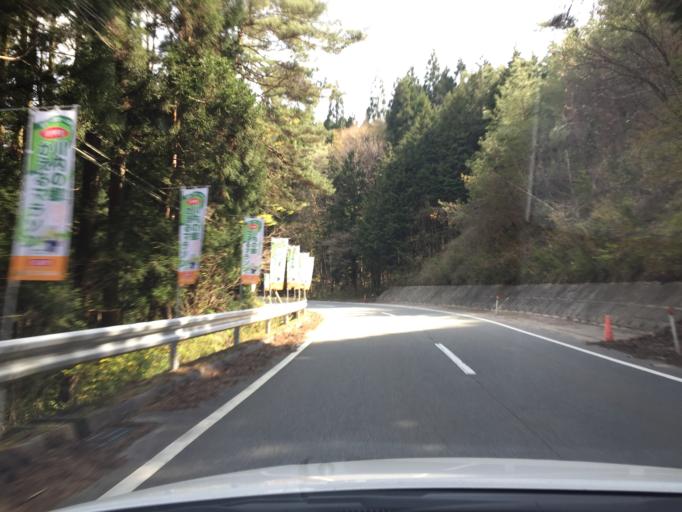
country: JP
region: Fukushima
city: Namie
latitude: 37.3027
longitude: 140.8359
